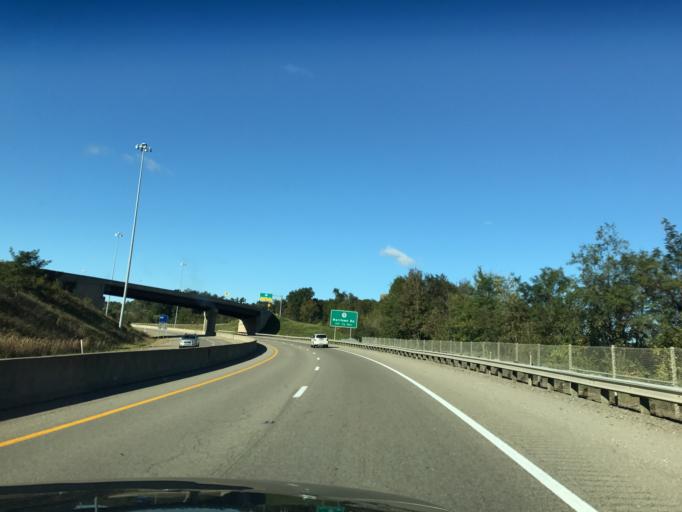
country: US
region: West Virginia
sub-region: Wood County
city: Parkersburg
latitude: 39.2639
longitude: -81.5709
